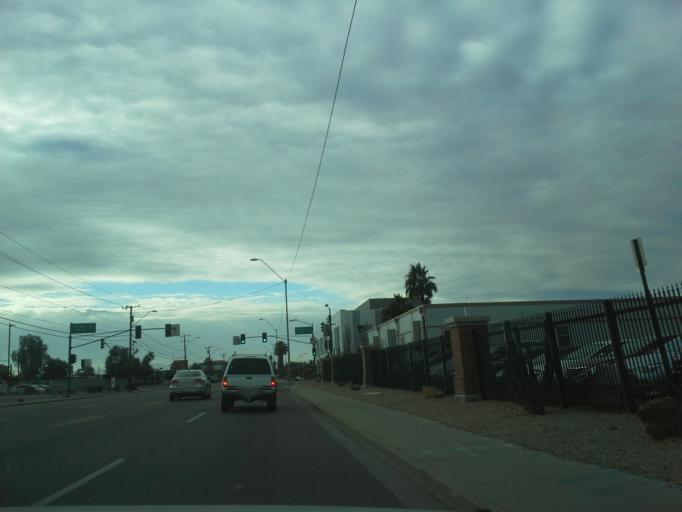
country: US
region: Arizona
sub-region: Maricopa County
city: Phoenix
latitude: 33.4989
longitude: -112.0651
